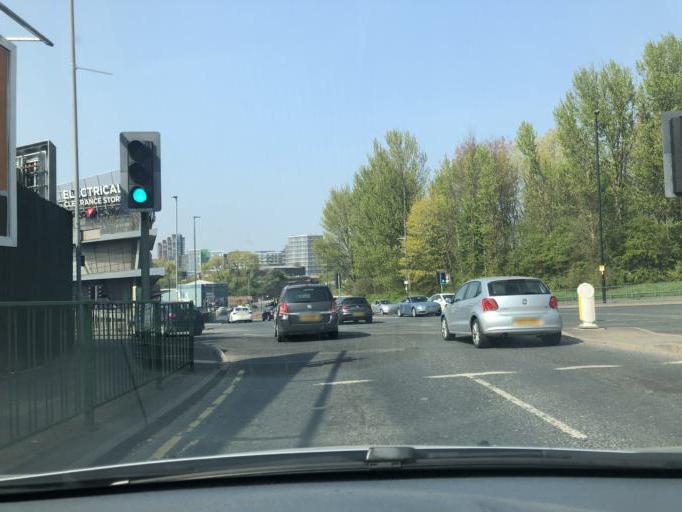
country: GB
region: England
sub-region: Manchester
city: Manchester
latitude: 53.4751
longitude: -2.2168
